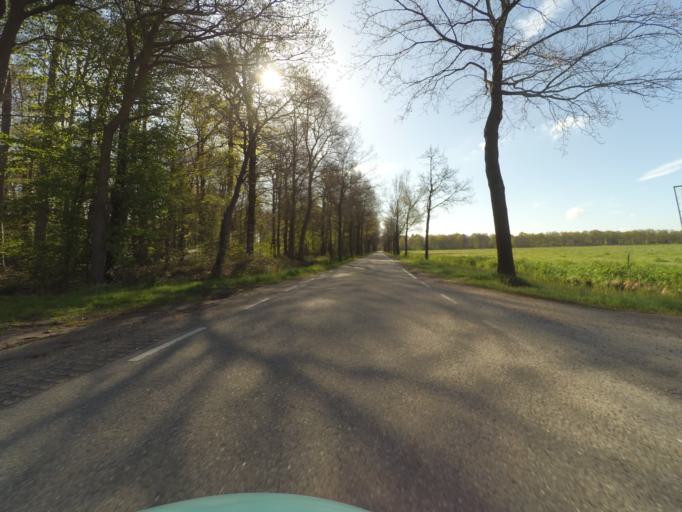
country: NL
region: Utrecht
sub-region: Gemeente Utrechtse Heuvelrug
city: Doorn
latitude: 52.0254
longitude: 5.3185
